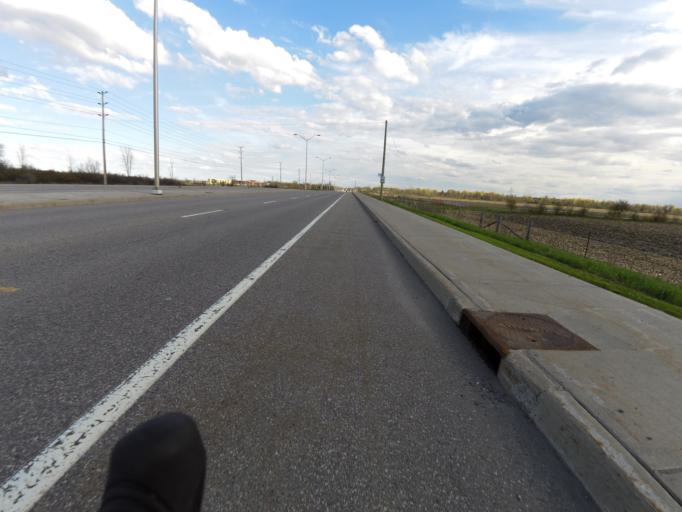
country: CA
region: Ontario
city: Ottawa
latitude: 45.2970
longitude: -75.6768
